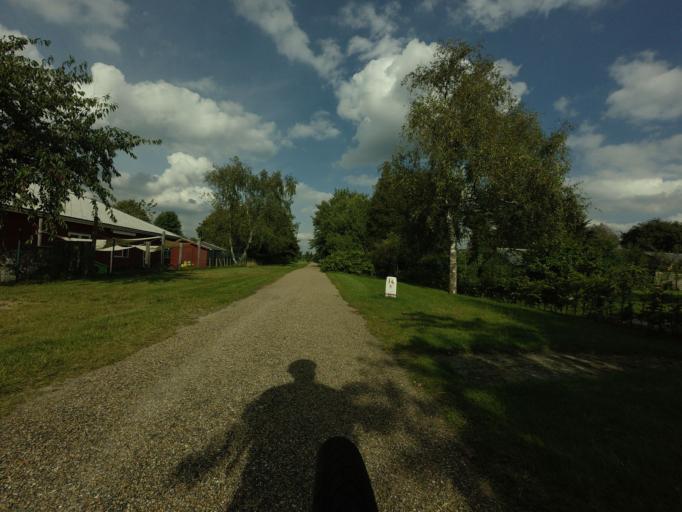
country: DK
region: Central Jutland
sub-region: Herning Kommune
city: Sunds
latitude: 56.2363
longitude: 9.0898
